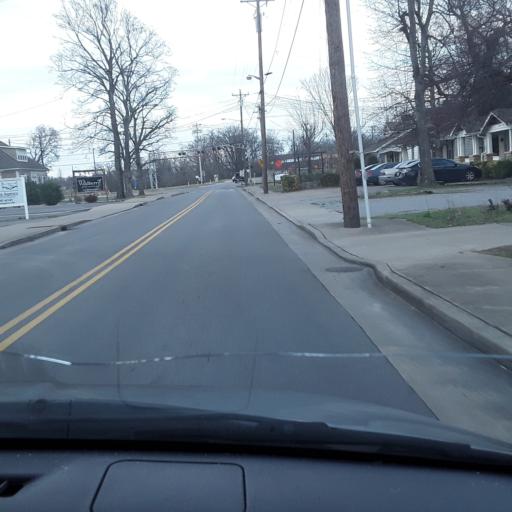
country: US
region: Tennessee
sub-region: Wilson County
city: Lebanon
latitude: 36.2102
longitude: -86.2960
